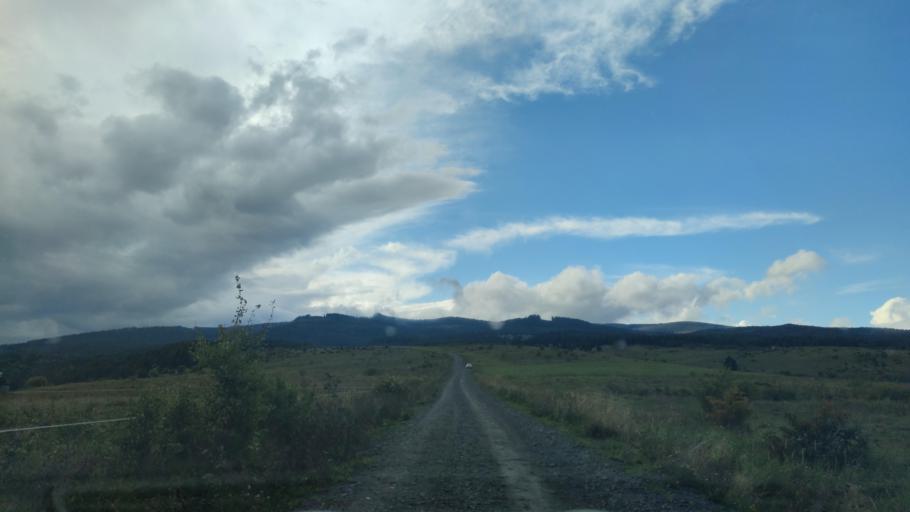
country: RO
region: Harghita
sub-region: Comuna Remetea
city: Remetea
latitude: 46.8163
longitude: 25.3735
